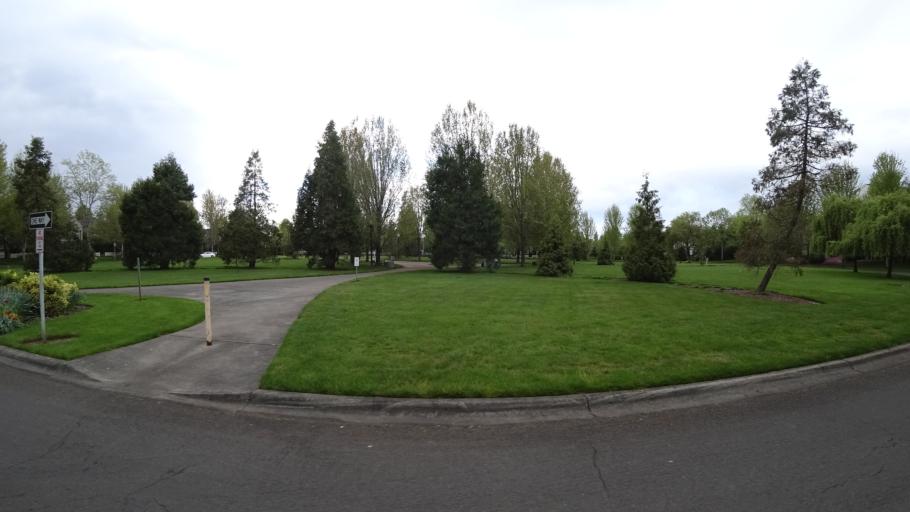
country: US
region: Oregon
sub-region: Washington County
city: Hillsboro
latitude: 45.5435
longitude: -122.9701
